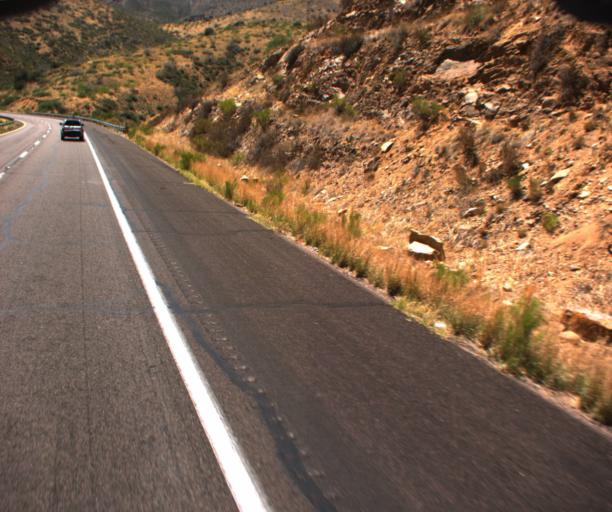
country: US
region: Arizona
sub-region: Gila County
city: Tonto Basin
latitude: 33.9610
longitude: -111.3961
